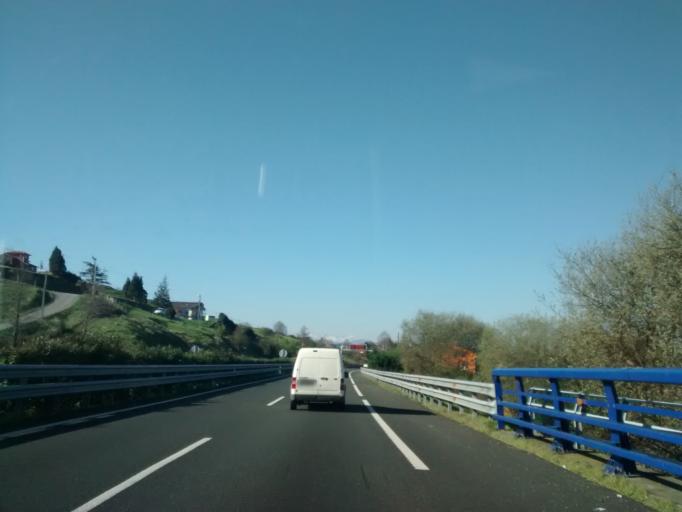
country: ES
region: Cantabria
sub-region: Provincia de Cantabria
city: Santa Cruz de Bezana
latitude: 43.4282
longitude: -3.9312
